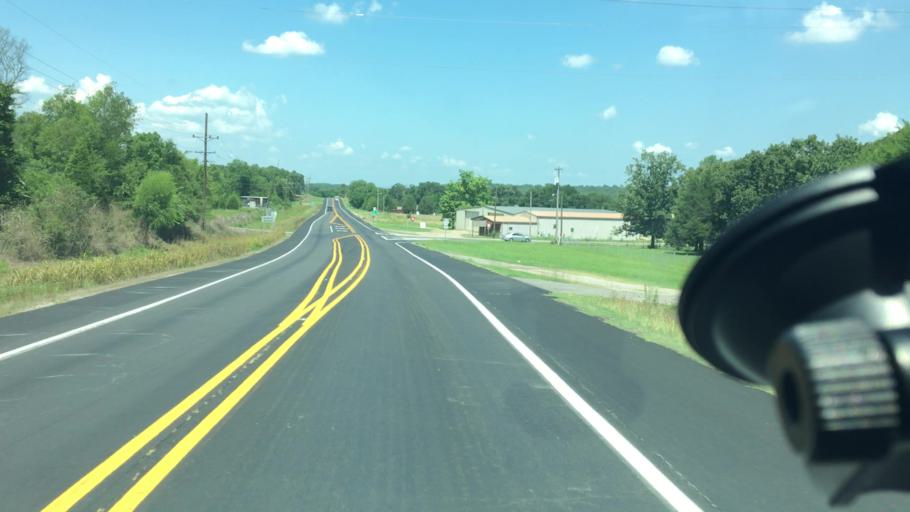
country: US
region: Arkansas
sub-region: Sebastian County
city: Lavaca
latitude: 35.3016
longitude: -94.1614
